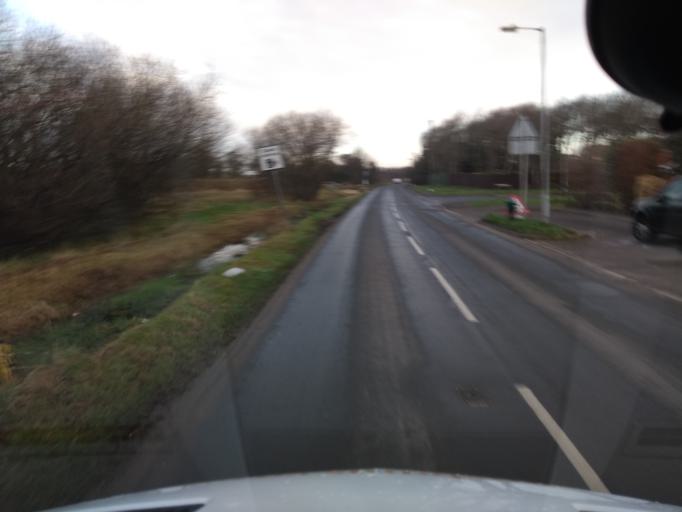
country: GB
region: England
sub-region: Somerset
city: Burnham-on-Sea
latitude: 51.2670
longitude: -3.0121
